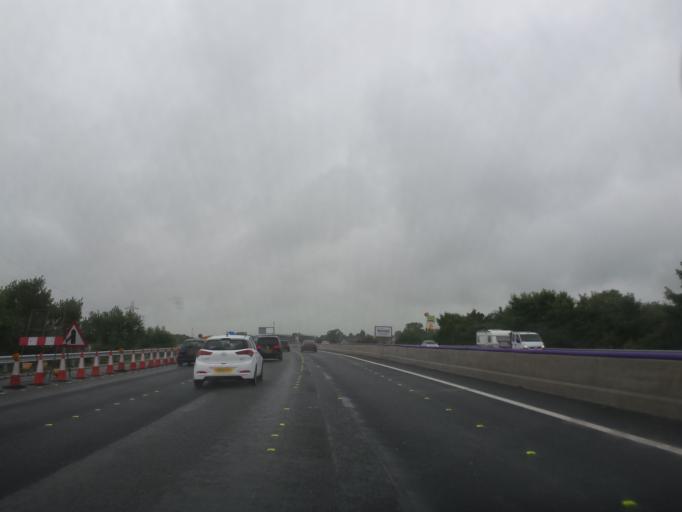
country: GB
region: England
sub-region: Derbyshire
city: Staveley
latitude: 53.2446
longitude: -1.3319
